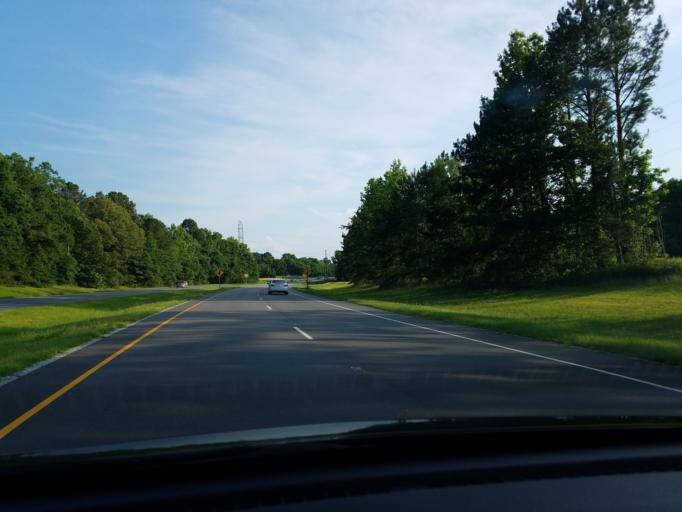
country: US
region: North Carolina
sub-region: Durham County
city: Gorman
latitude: 36.1240
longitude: -78.9008
